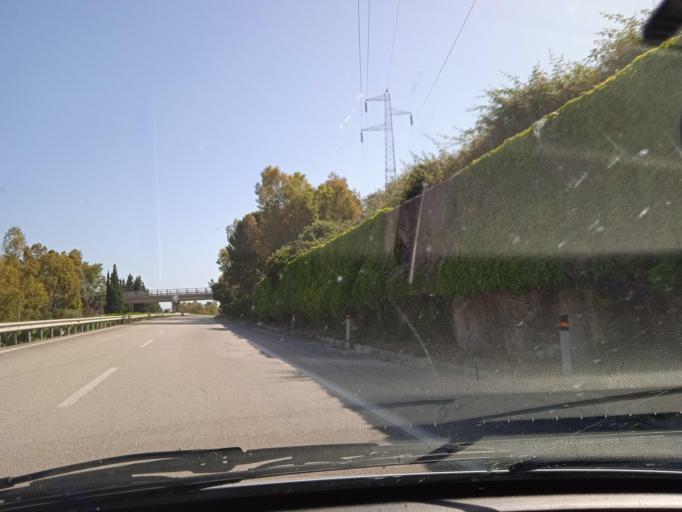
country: IT
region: Sicily
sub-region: Messina
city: Torrenova
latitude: 38.0887
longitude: 14.6937
